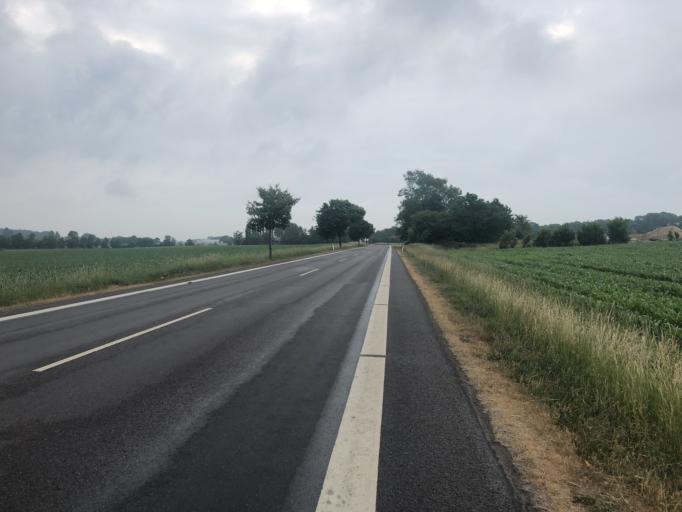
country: DK
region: Capital Region
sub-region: Bornholm Kommune
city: Akirkeby
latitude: 55.1528
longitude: 14.9126
